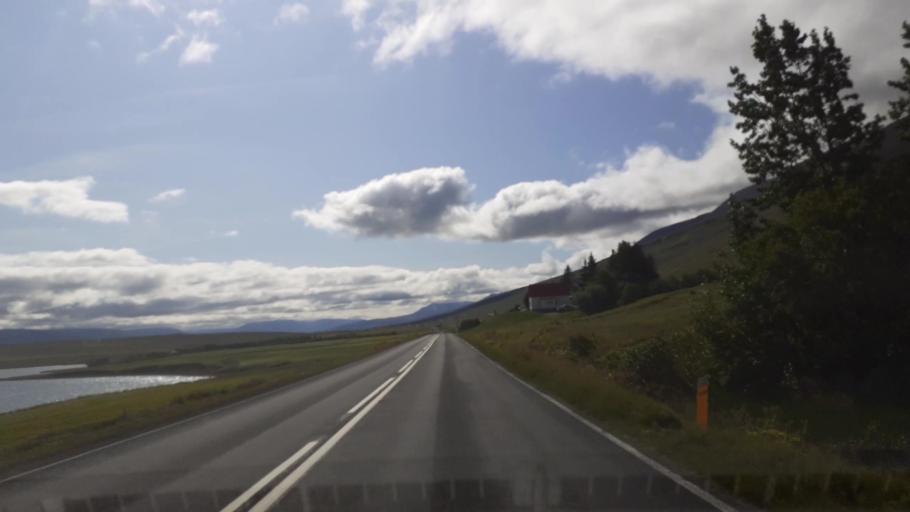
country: IS
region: Northeast
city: Akureyri
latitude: 65.8722
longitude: -18.2636
